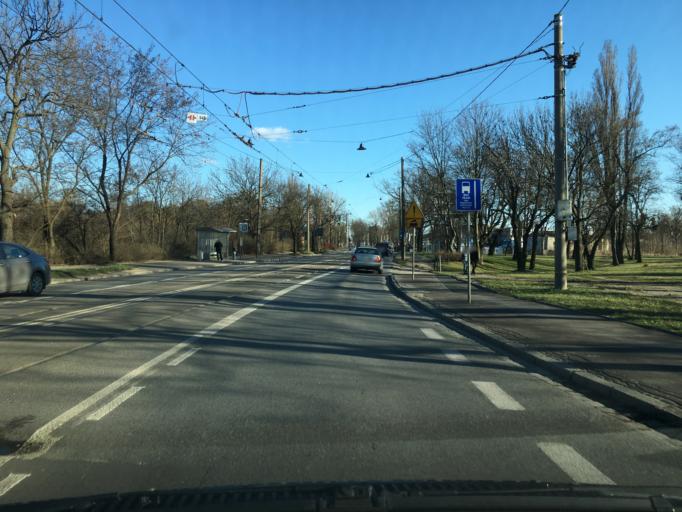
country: PL
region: Lower Silesian Voivodeship
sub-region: Powiat wroclawski
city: Wroclaw
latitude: 51.0854
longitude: 17.0714
